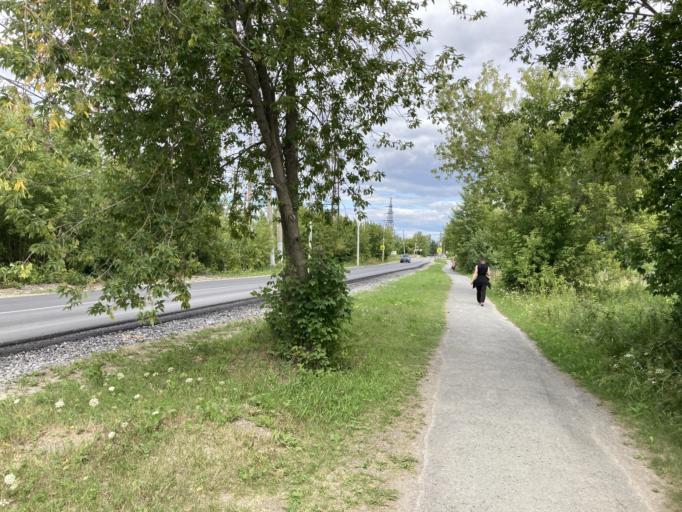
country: RU
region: Sverdlovsk
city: Bogdanovich
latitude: 56.7797
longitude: 62.0635
